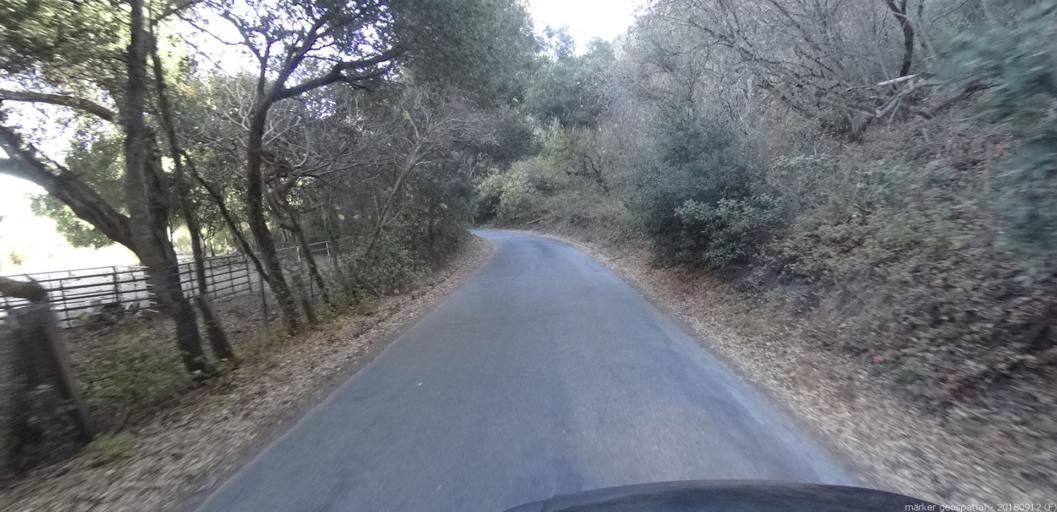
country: US
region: California
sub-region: Monterey County
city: Carmel Valley Village
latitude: 36.5384
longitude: -121.7374
